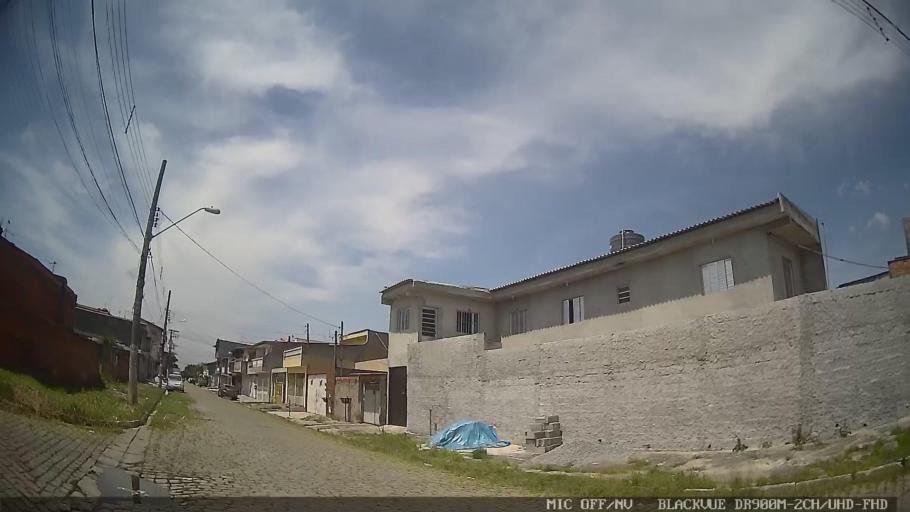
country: BR
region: Sao Paulo
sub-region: Suzano
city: Suzano
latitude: -23.5189
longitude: -46.3054
